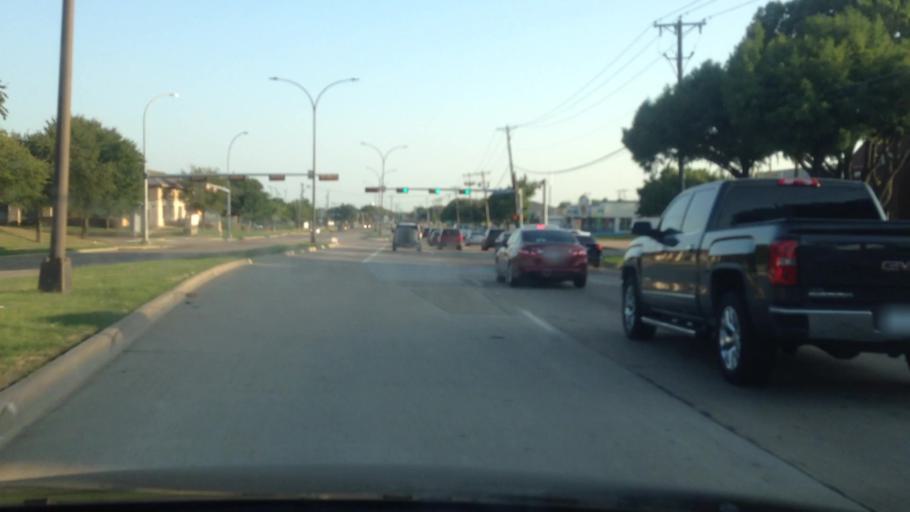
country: US
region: Texas
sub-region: Tarrant County
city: Dalworthington Gardens
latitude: 32.6749
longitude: -97.1151
